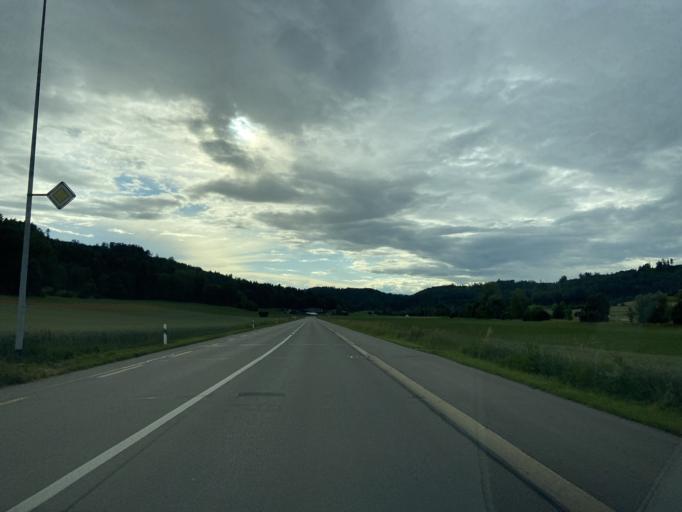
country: CH
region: Zurich
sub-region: Bezirk Winterthur
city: Elgg
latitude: 47.5003
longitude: 8.8506
